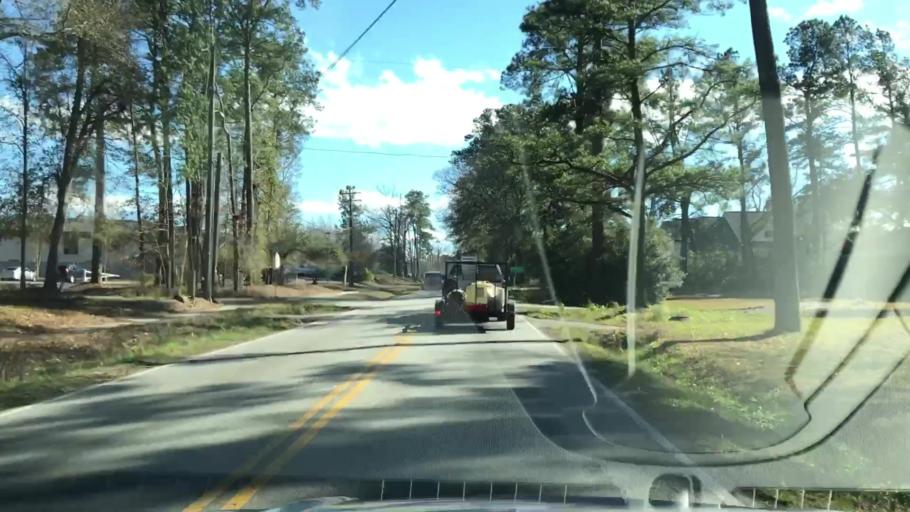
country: US
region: South Carolina
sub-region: Dorchester County
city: Summerville
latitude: 33.0261
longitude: -80.2432
